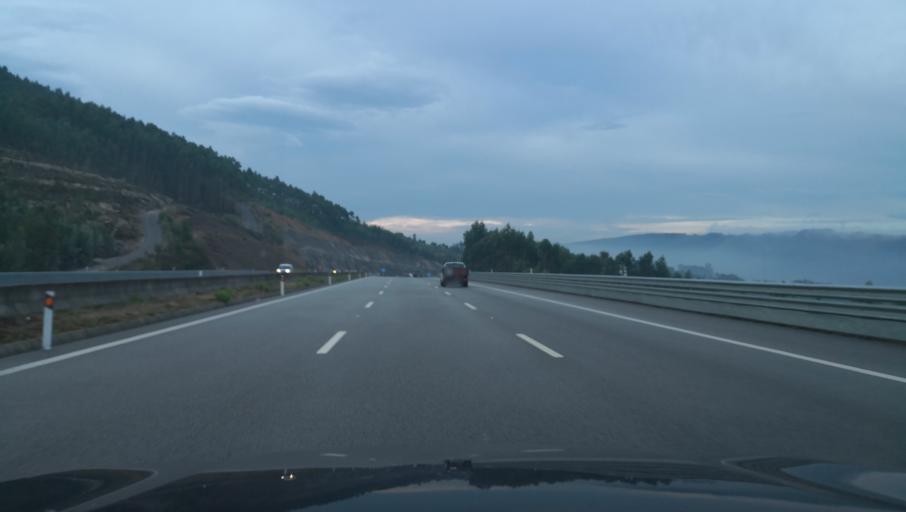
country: PT
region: Porto
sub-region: Paredes
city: Recarei
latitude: 41.1164
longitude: -8.4329
